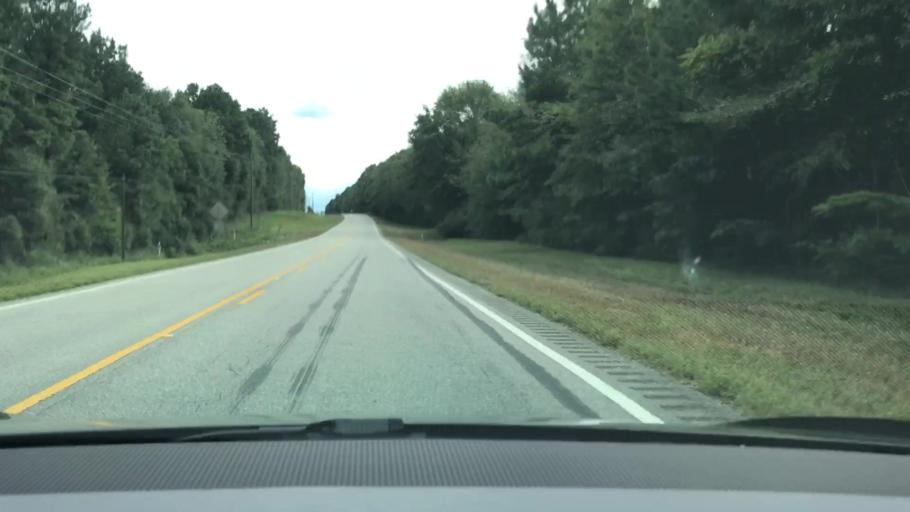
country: US
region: Alabama
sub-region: Pike County
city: Troy
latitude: 31.6437
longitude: -85.9707
